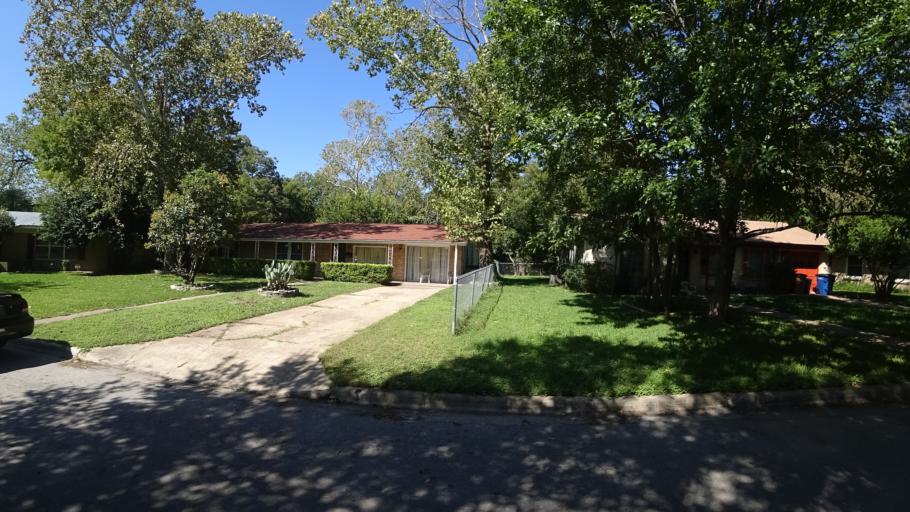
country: US
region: Texas
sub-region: Travis County
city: Austin
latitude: 30.3141
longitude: -97.6941
